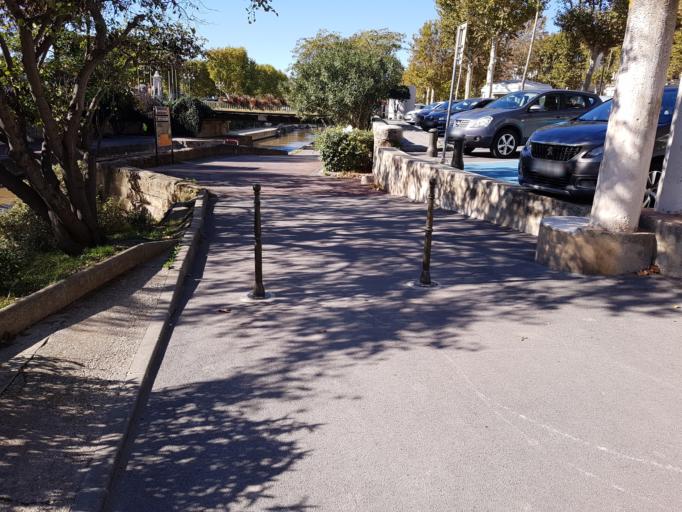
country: FR
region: Languedoc-Roussillon
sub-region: Departement de l'Aude
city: Narbonne
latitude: 43.1814
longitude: 3.0075
